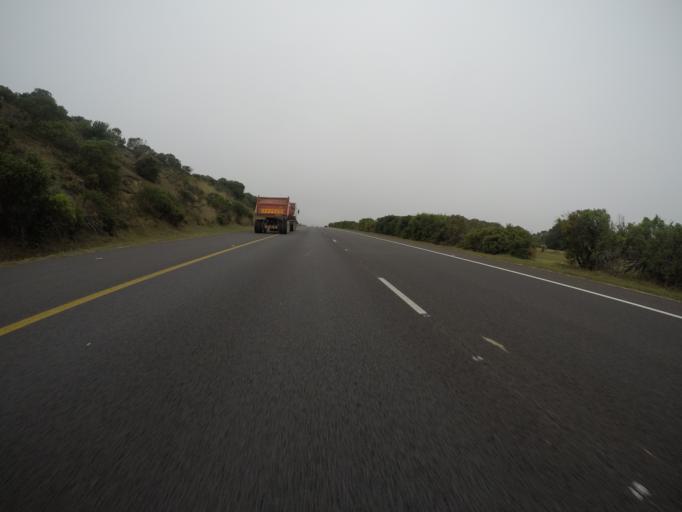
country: ZA
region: Western Cape
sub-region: Eden District Municipality
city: Mossel Bay
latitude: -34.0605
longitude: 22.1933
